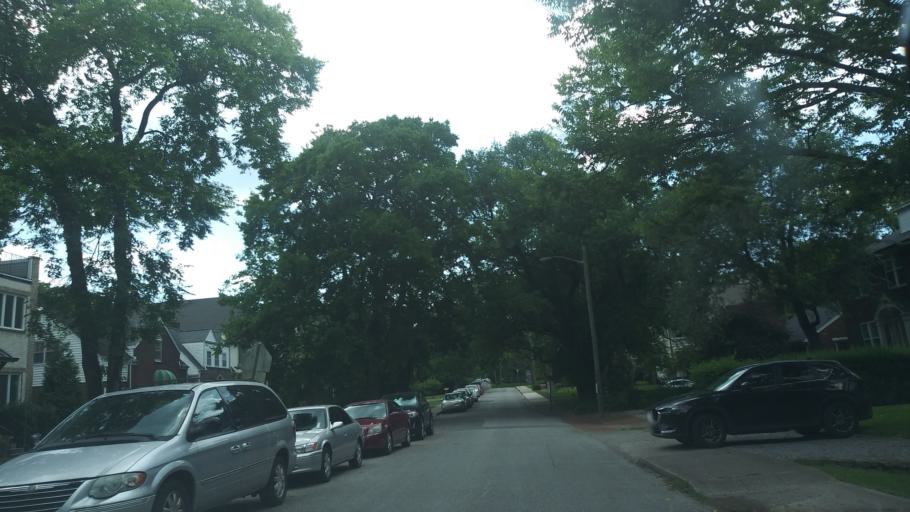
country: US
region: Tennessee
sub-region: Davidson County
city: Nashville
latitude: 36.1360
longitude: -86.8095
